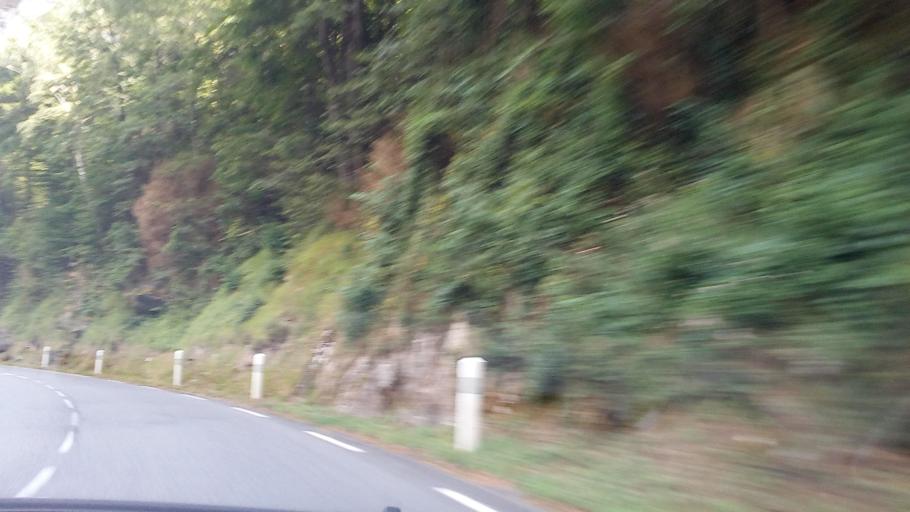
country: FR
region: Aquitaine
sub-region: Departement des Pyrenees-Atlantiques
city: Arette
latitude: 42.9600
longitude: -0.6099
